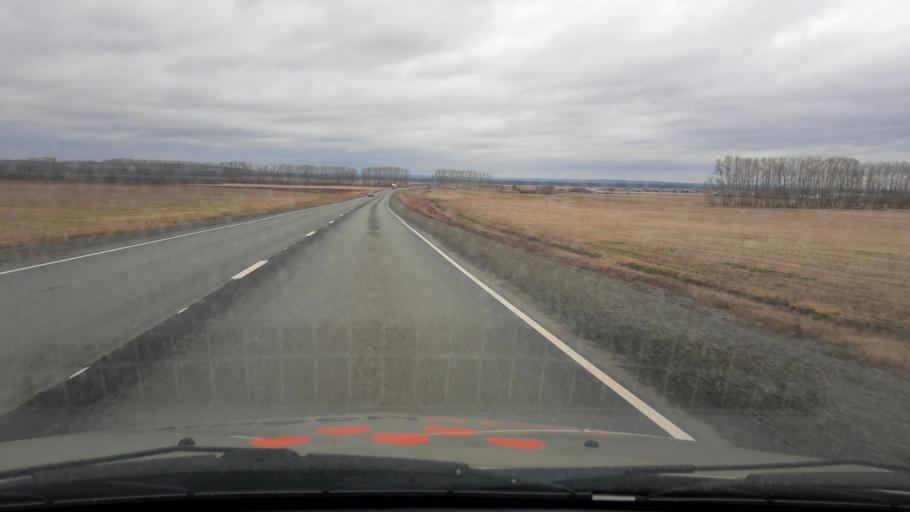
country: RU
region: Bashkortostan
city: Avdon
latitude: 54.8612
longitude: 55.7037
